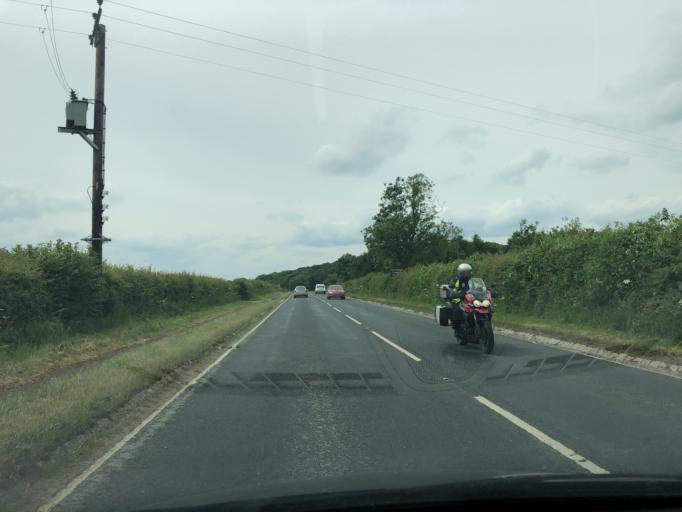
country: GB
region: England
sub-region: North Yorkshire
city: Great Habton
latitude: 54.2590
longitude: -0.8650
